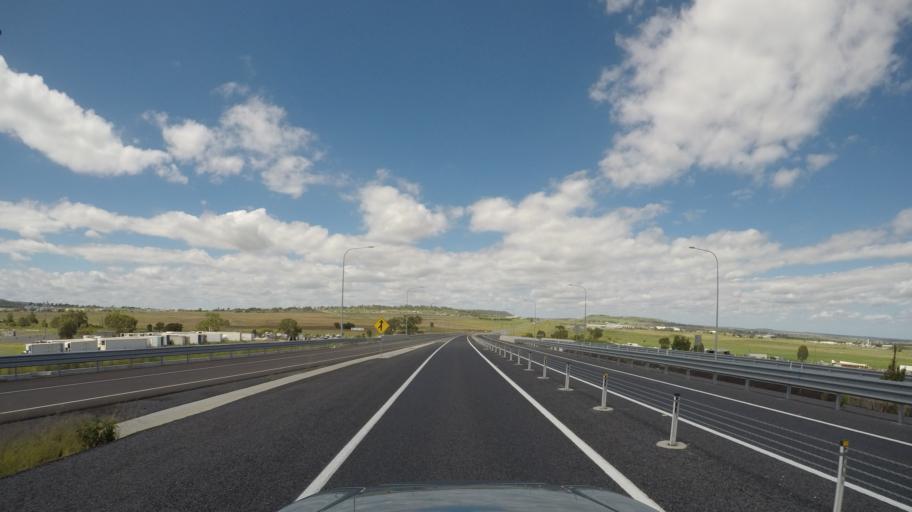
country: AU
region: Queensland
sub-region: Toowoomba
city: Wilsonton Heights
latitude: -27.5285
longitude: 151.8584
